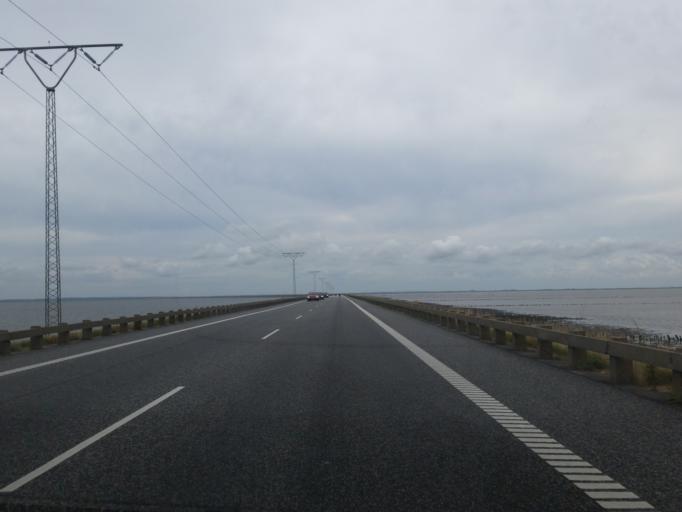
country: DK
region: South Denmark
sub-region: Tonder Kommune
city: Sherrebek
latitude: 55.1493
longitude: 8.5870
